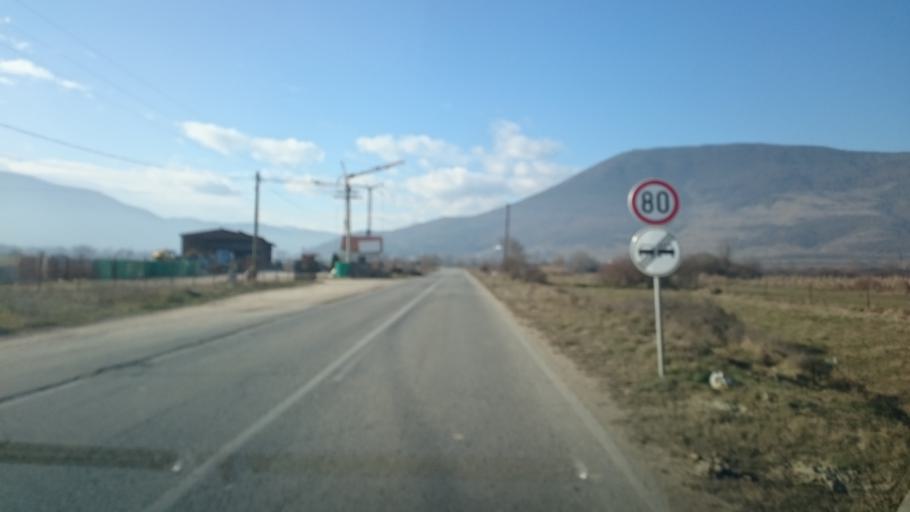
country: MK
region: Plasnica
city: Lisicani
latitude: 41.4699
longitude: 21.0491
